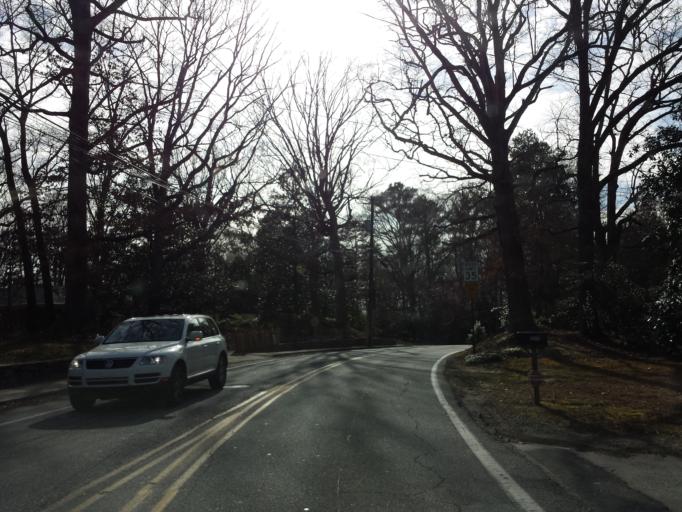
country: US
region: Georgia
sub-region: Cobb County
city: Vinings
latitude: 33.8309
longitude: -84.4274
